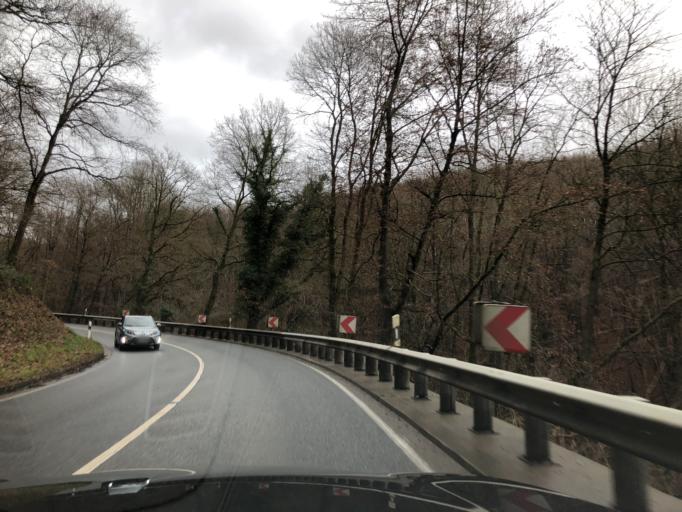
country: DE
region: Rheinland-Pfalz
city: Bruchhausen
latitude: 50.6005
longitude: 7.2376
